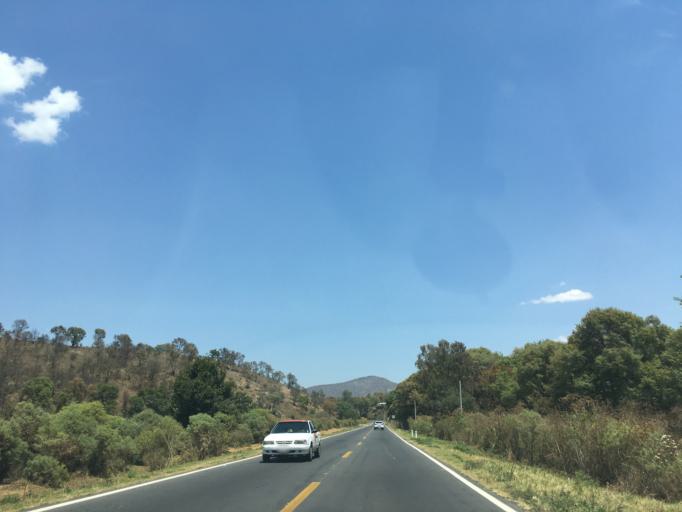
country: MX
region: Michoacan
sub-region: Chilchota
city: Tacuro (Santa Maria Tacuro)
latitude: 19.8395
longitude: -102.0329
